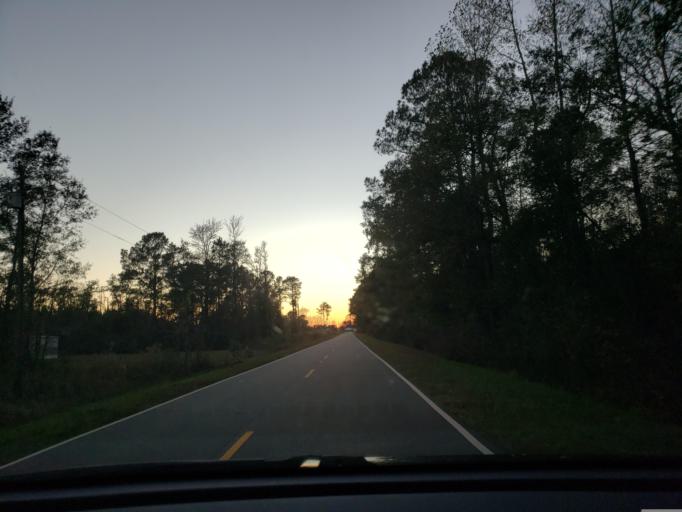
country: US
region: North Carolina
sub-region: Duplin County
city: Beulaville
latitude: 34.7534
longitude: -77.6988
